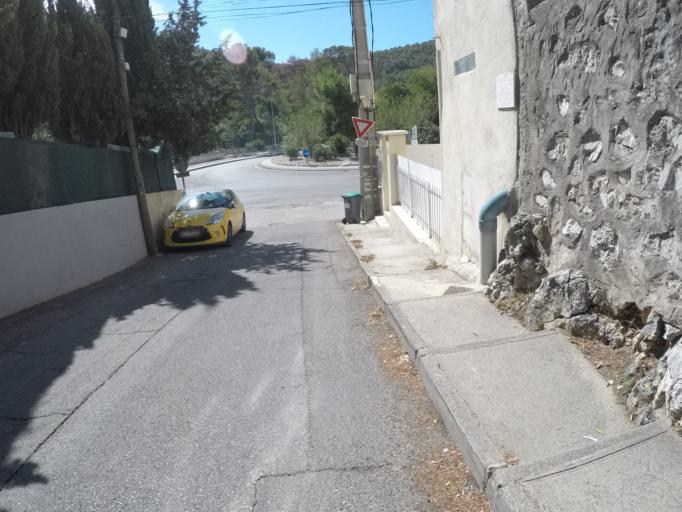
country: FR
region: Provence-Alpes-Cote d'Azur
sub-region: Departement des Bouches-du-Rhone
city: Marseille 09
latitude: 43.2451
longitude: 5.4276
